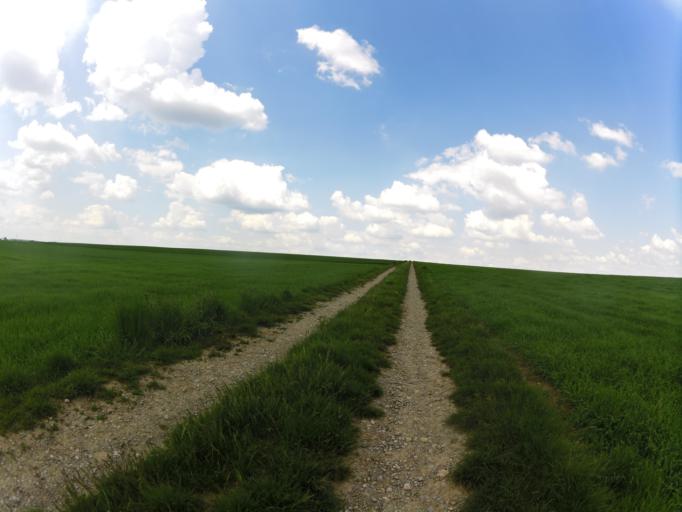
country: DE
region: Bavaria
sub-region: Regierungsbezirk Unterfranken
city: Sulzdorf
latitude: 49.6270
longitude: 9.9130
